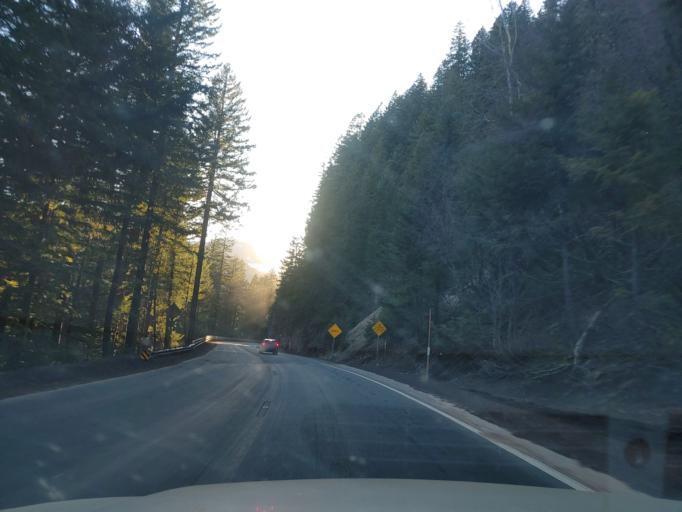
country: US
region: Oregon
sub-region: Lane County
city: Oakridge
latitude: 43.6139
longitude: -122.1289
